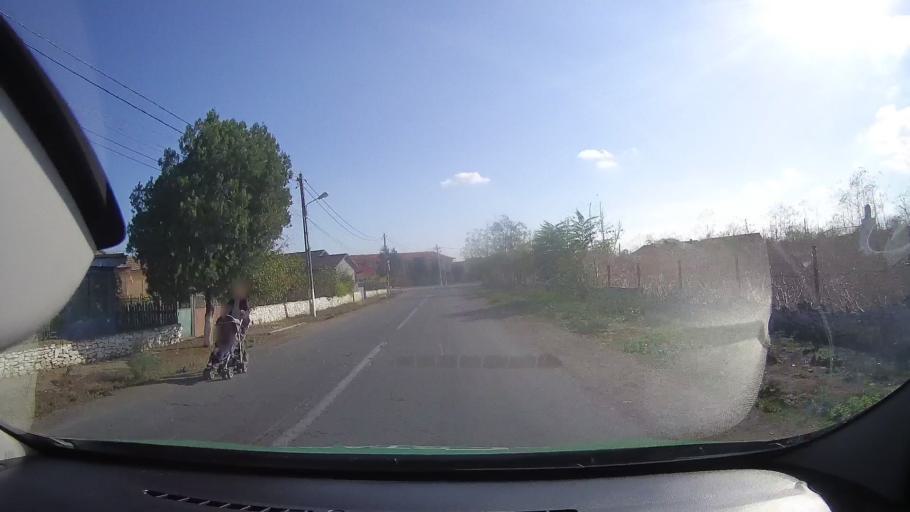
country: RO
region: Constanta
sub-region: Comuna Mihai Viteazu
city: Mihai Viteazu
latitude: 44.6302
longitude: 28.7310
